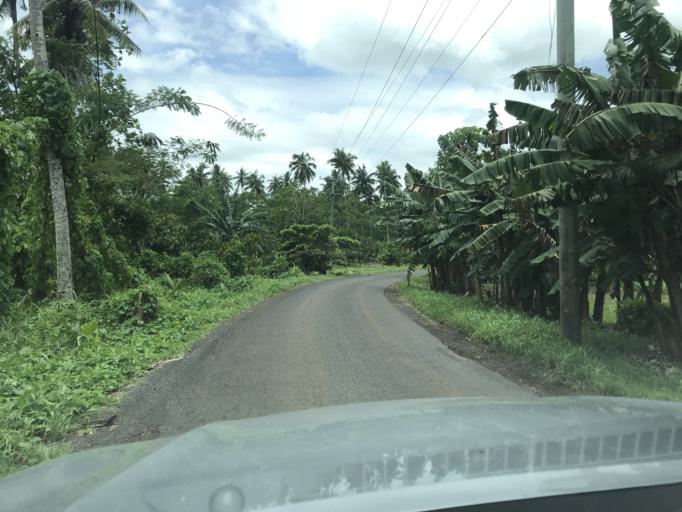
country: WS
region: Tuamasaga
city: Afenga
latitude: -13.8162
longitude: -171.8855
